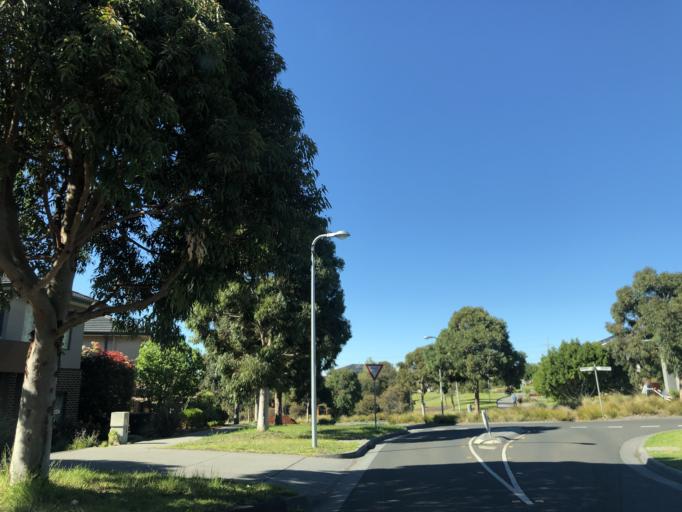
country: AU
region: Victoria
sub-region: Monash
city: Mulgrave
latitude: -37.9256
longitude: 145.1928
